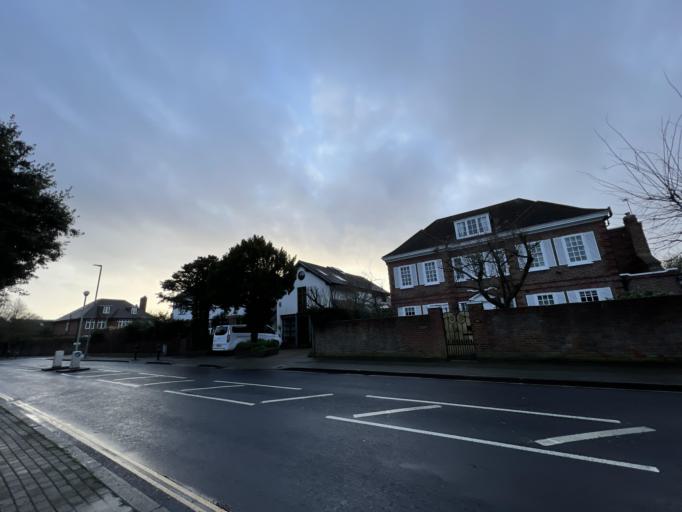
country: GB
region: England
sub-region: Greater London
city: Wandsworth
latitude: 51.4524
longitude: -0.2367
